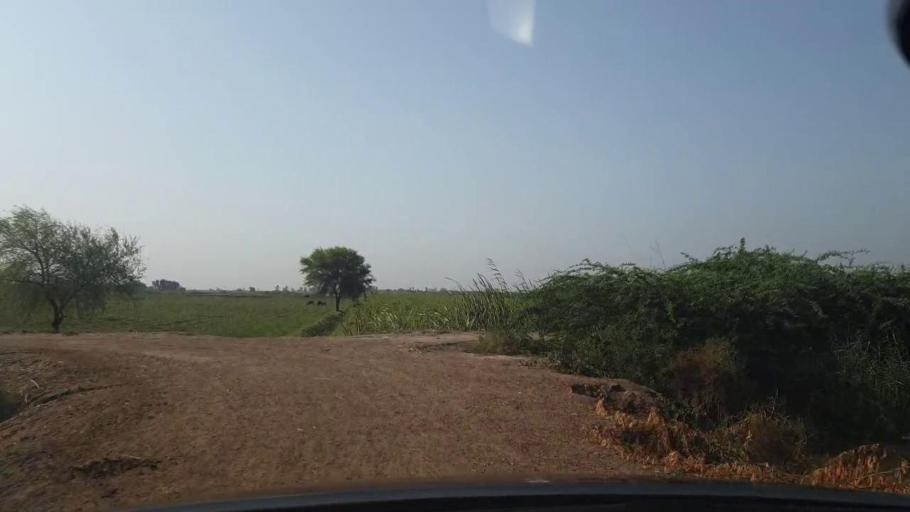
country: PK
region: Sindh
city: Kadhan
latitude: 24.6454
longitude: 69.1481
